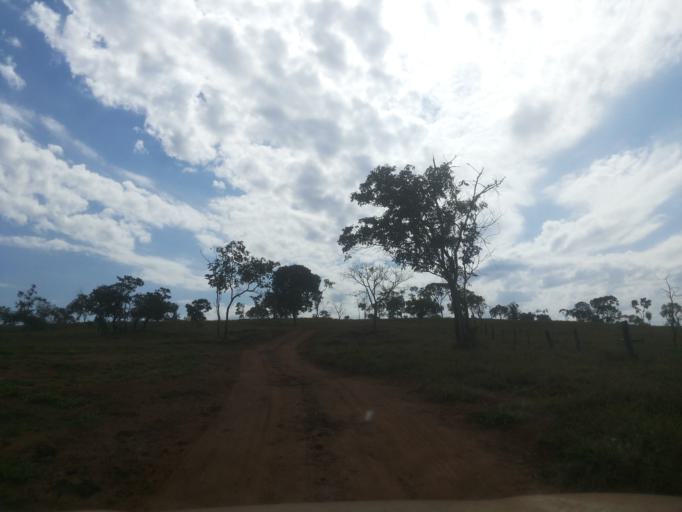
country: BR
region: Minas Gerais
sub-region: Ituiutaba
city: Ituiutaba
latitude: -19.0772
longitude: -49.3614
